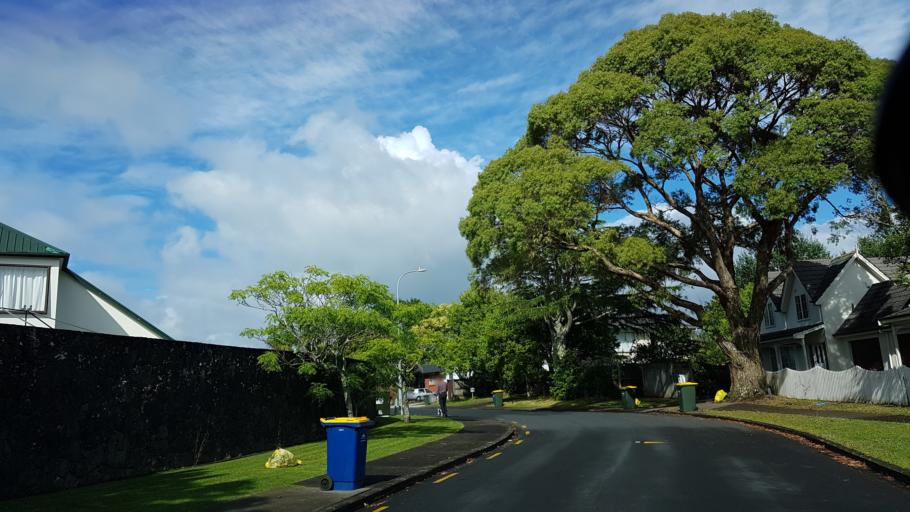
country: NZ
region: Auckland
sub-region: Auckland
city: North Shore
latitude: -36.7948
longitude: 174.7394
